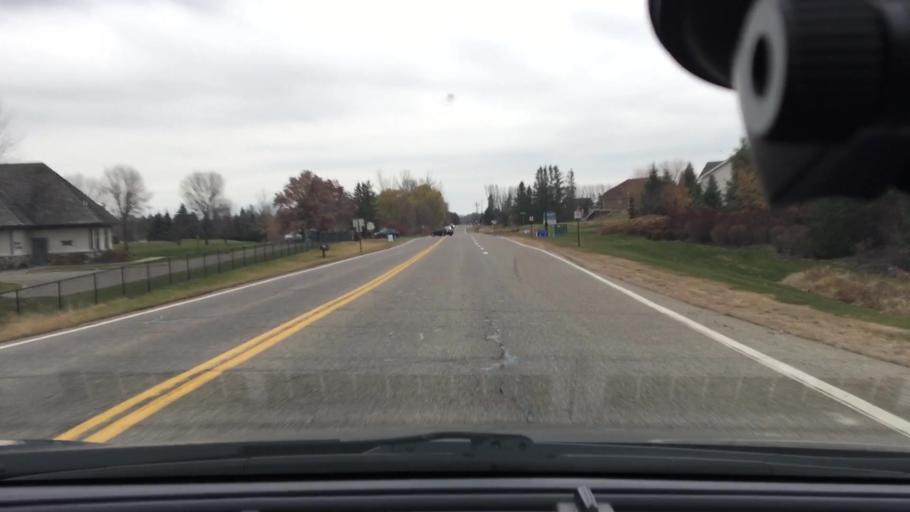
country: US
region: Minnesota
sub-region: Hennepin County
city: Corcoran
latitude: 45.0953
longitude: -93.5124
